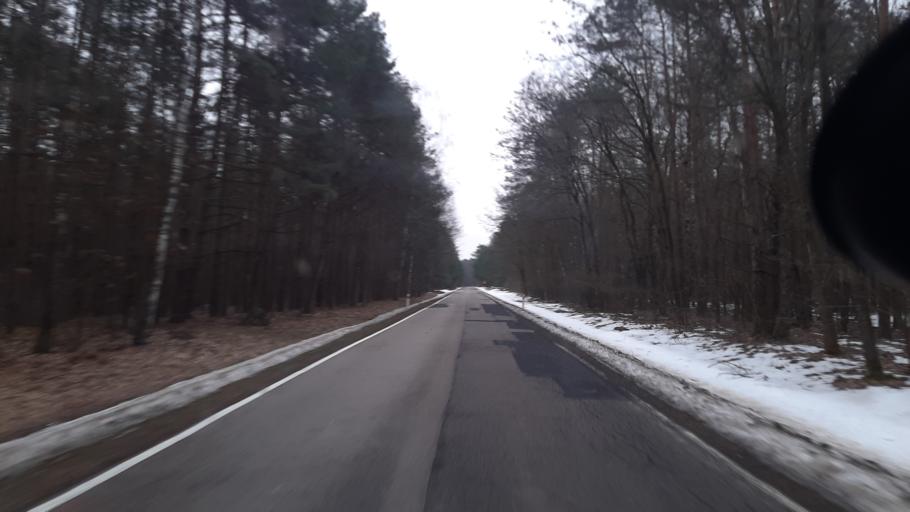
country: PL
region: Lublin Voivodeship
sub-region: Powiat wlodawski
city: Wlodawa
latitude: 51.4907
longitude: 23.6005
